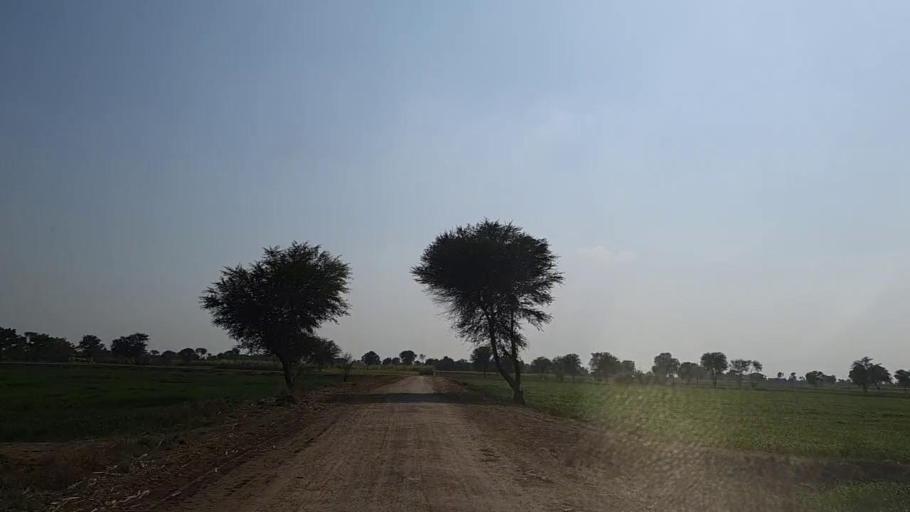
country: PK
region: Sindh
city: Daur
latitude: 26.4317
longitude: 68.2344
